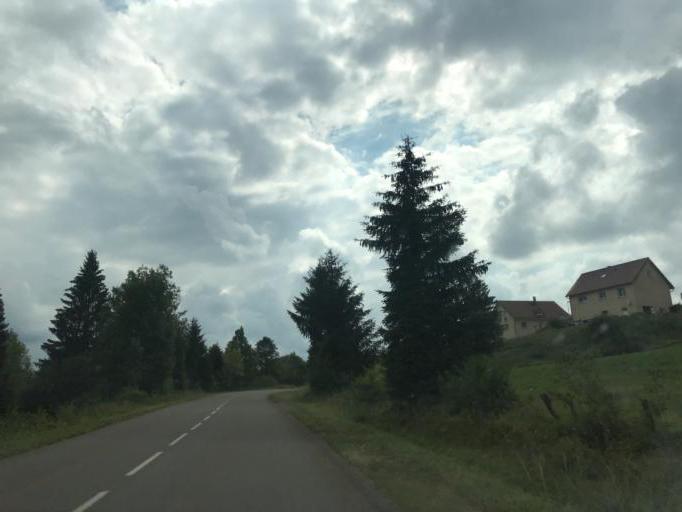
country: FR
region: Franche-Comte
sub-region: Departement du Jura
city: Longchaumois
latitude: 46.5000
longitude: 5.9058
